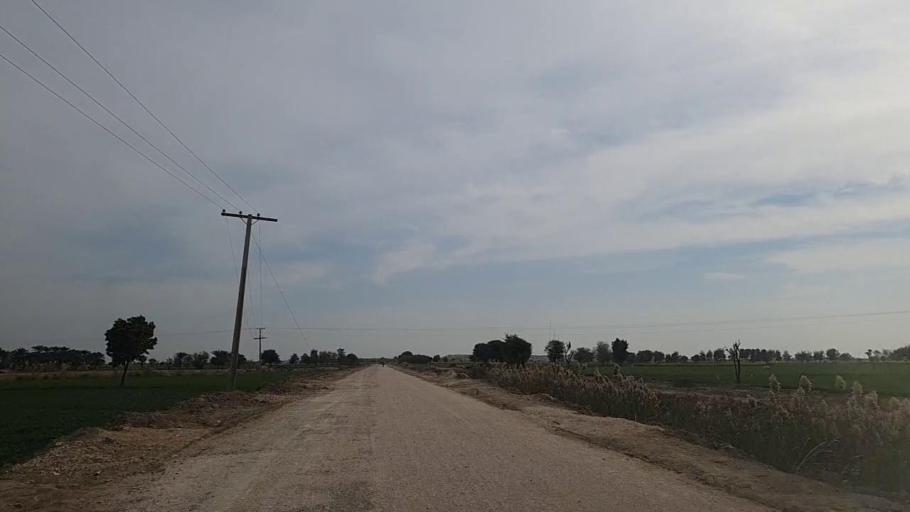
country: PK
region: Sindh
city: Jam Sahib
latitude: 26.4099
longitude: 68.4922
